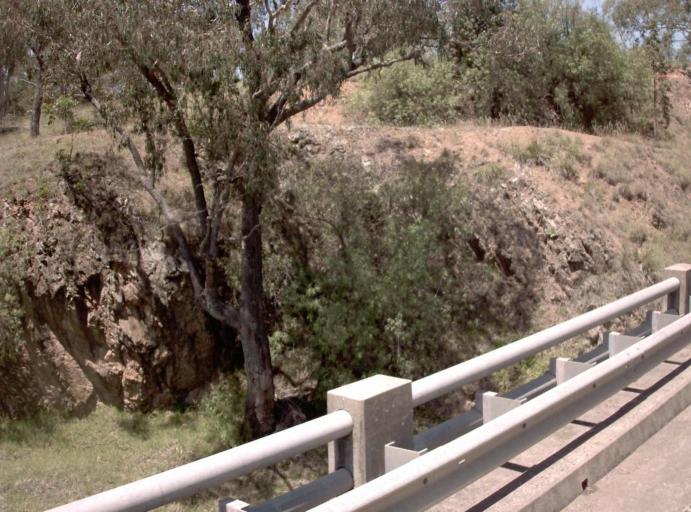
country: AU
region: Victoria
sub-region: East Gippsland
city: Bairnsdale
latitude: -37.3785
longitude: 147.8311
